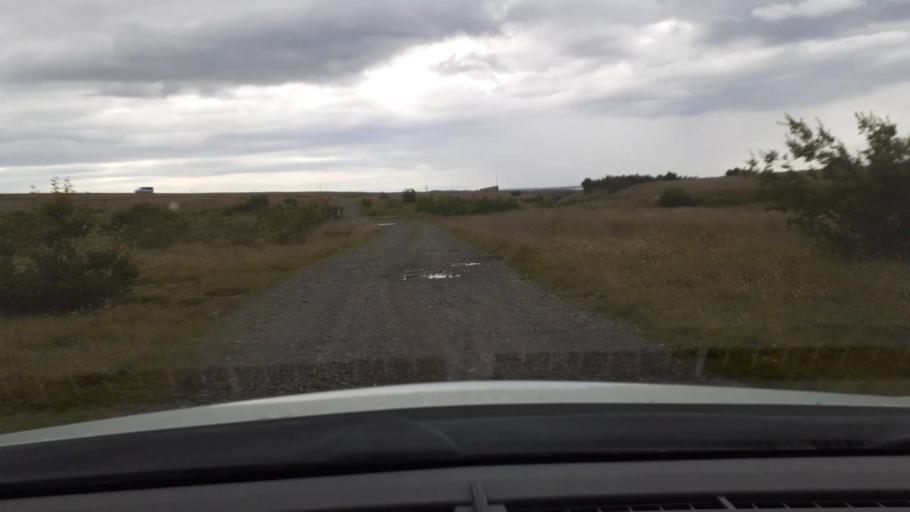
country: IS
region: West
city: Borgarnes
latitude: 64.4627
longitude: -21.9585
